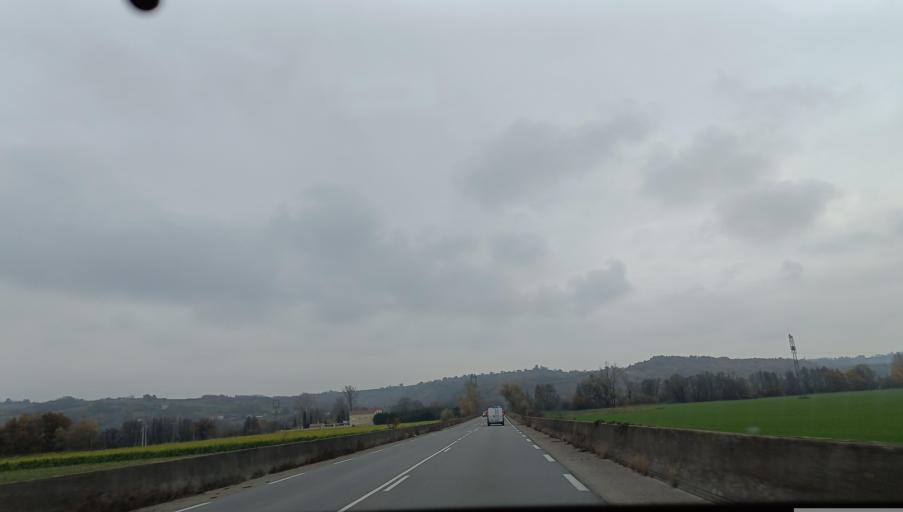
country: FR
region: Rhone-Alpes
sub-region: Departement de l'Isere
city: Pont-Eveque
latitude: 45.5340
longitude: 4.9287
